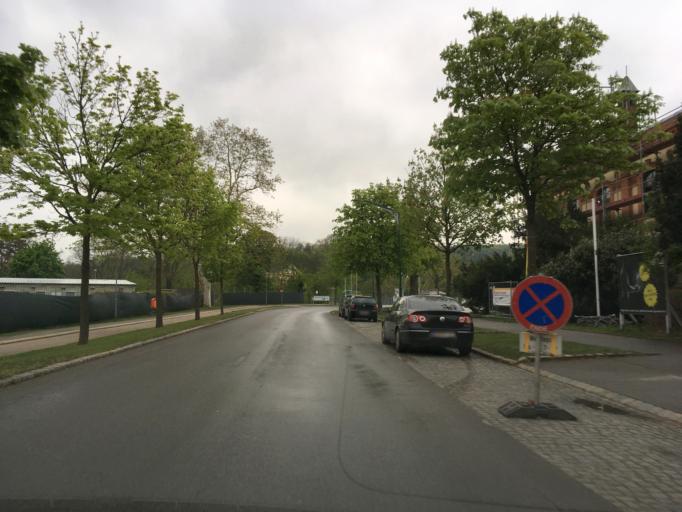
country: AT
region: Burgenland
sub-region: Politischer Bezirk Neusiedl am See
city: Bruckneudorf
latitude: 48.0182
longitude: 16.7781
